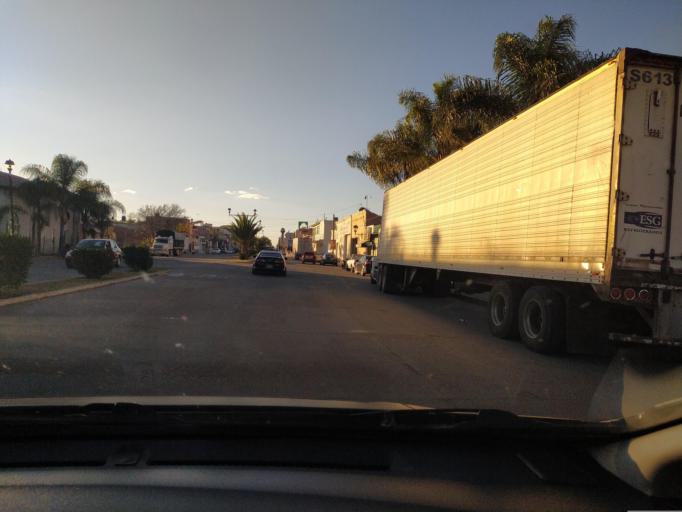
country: MX
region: Jalisco
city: San Julian
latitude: 21.0087
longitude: -102.1710
